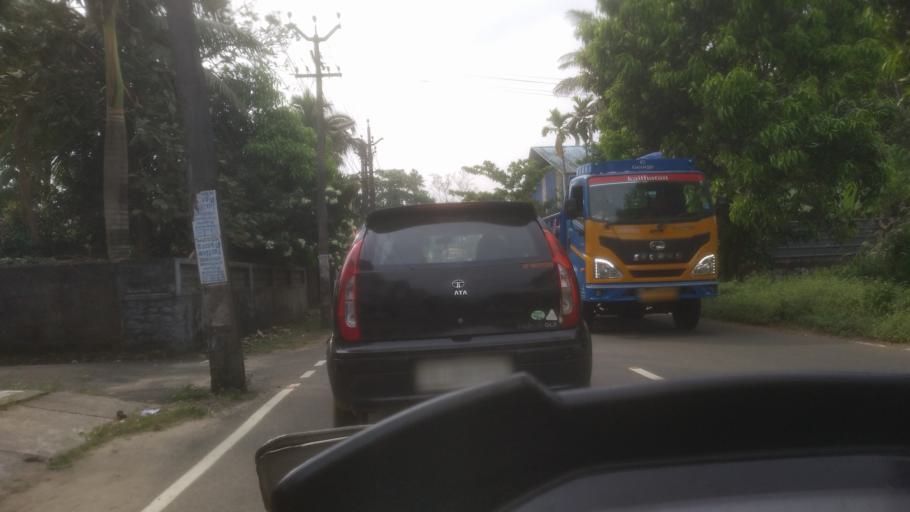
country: IN
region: Kerala
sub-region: Ernakulam
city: Angamali
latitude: 10.1634
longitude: 76.4069
